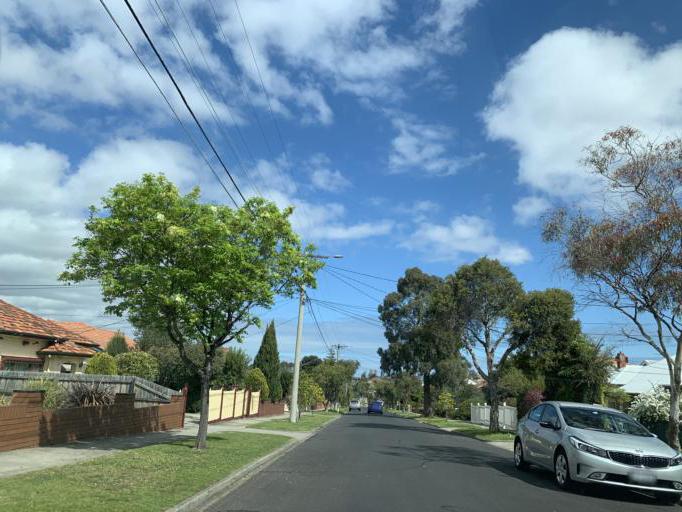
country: AU
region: Victoria
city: Thornbury
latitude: -37.7391
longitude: 144.9863
